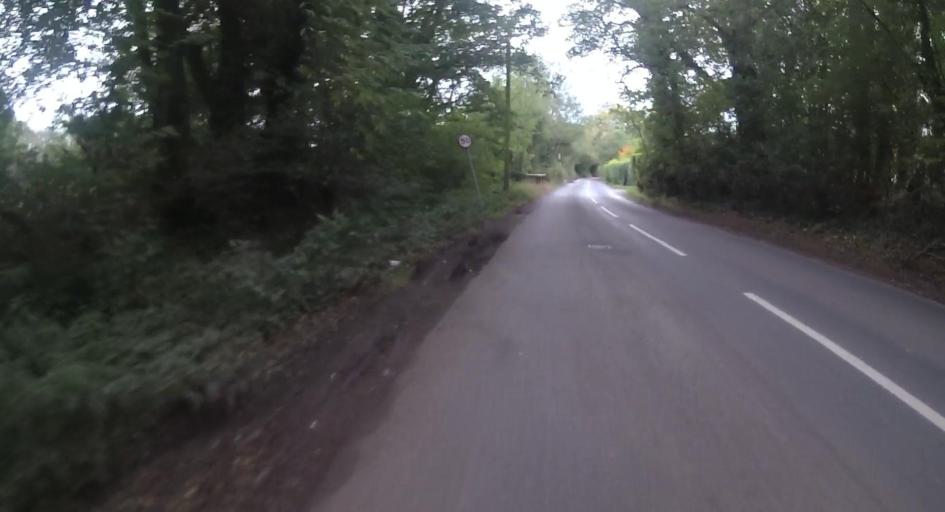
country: GB
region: England
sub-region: Hampshire
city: Fleet
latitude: 51.2488
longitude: -0.8617
